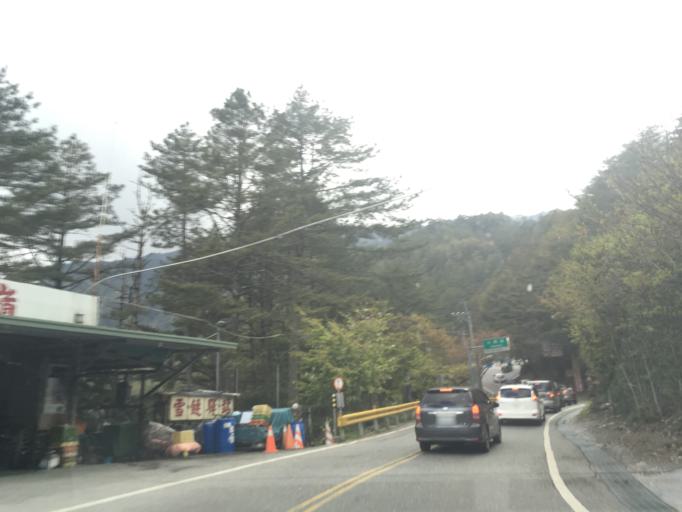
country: TW
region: Taiwan
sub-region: Hualien
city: Hualian
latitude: 24.1798
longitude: 121.3103
